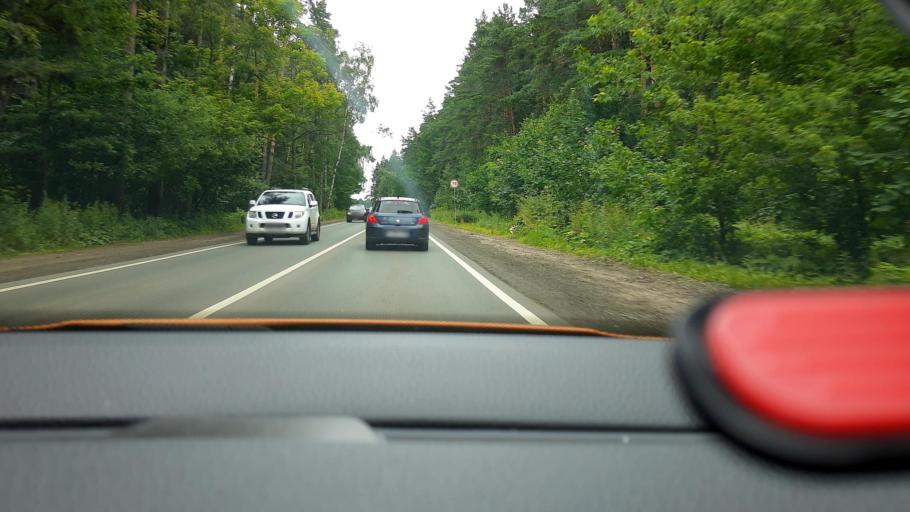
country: RU
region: Moskovskaya
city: Pirogovskiy
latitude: 55.9931
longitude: 37.7275
